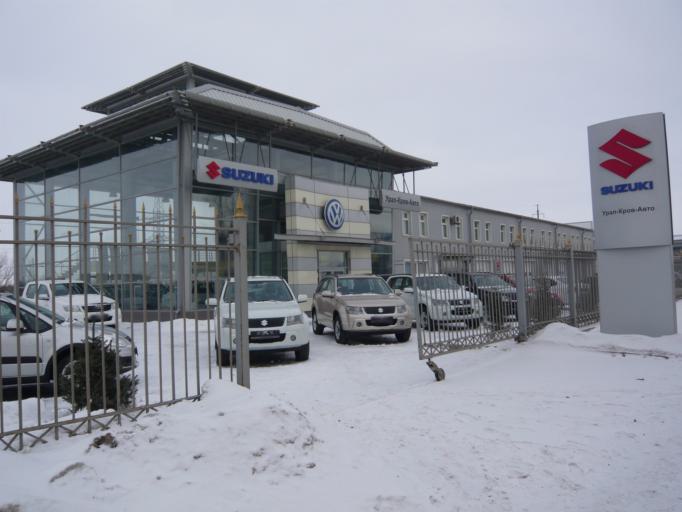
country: KZ
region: Batys Qazaqstan
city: Oral
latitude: 51.2465
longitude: 51.3837
